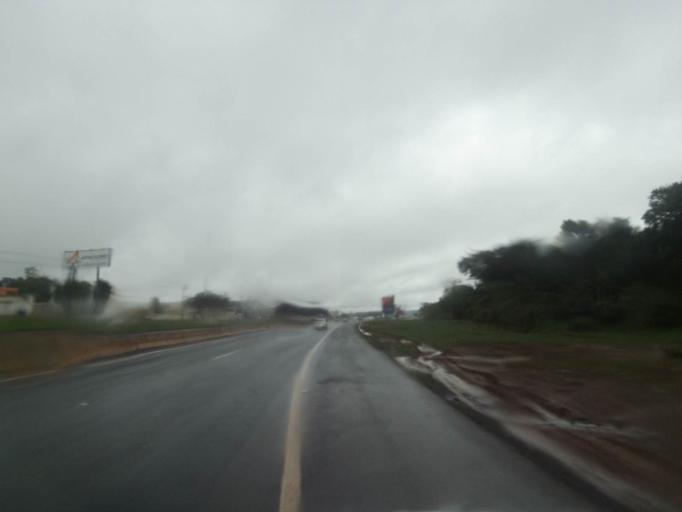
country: PY
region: Alto Parana
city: Ciudad del Este
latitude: -25.5096
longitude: -54.5762
